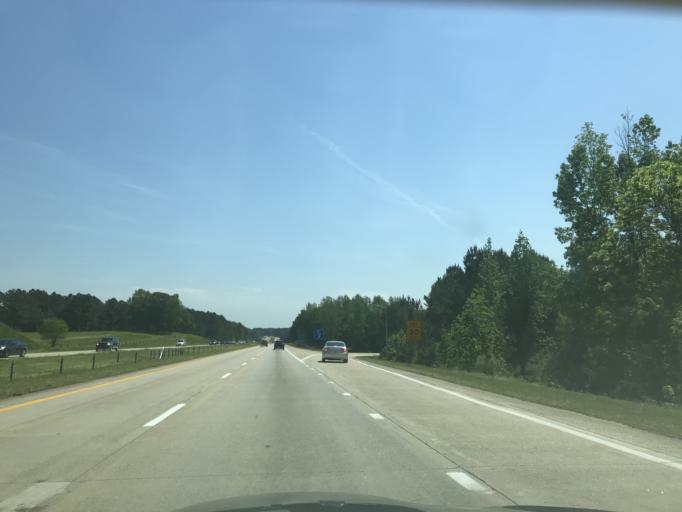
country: US
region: North Carolina
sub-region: Johnston County
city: Benson
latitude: 35.4395
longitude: -78.5344
